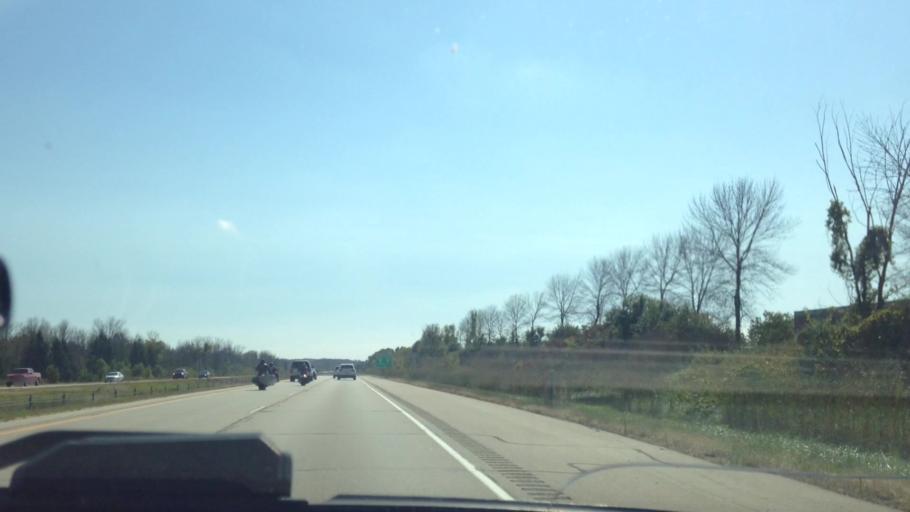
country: US
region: Wisconsin
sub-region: Ozaukee County
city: Thiensville
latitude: 43.2426
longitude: -87.9201
